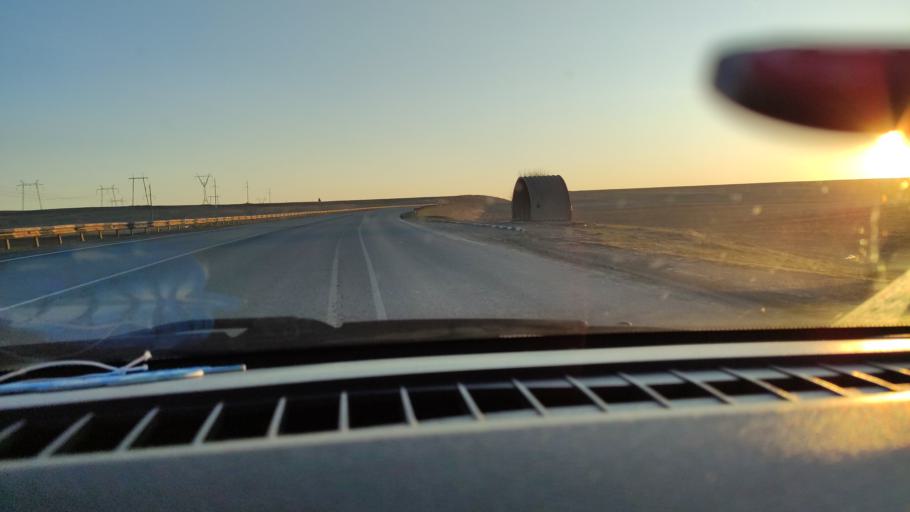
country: RU
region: Saratov
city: Sinodskoye
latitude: 51.9241
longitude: 46.5640
